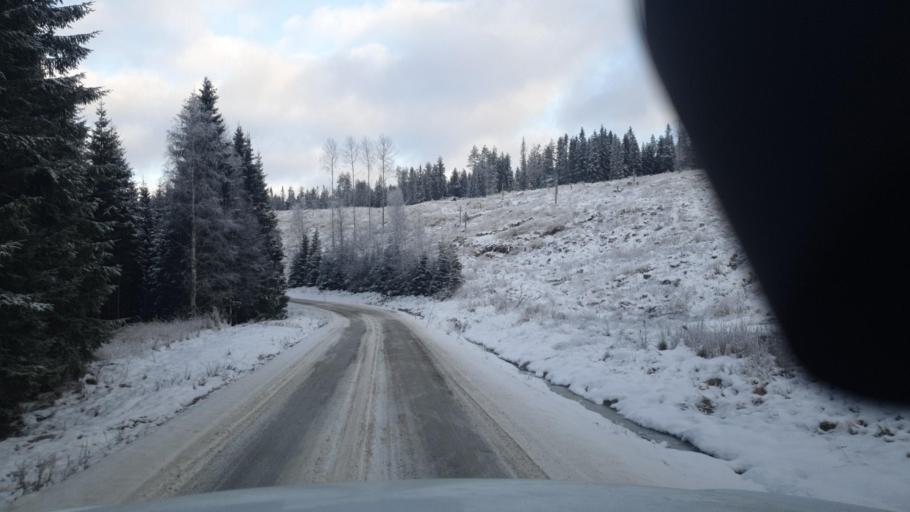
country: SE
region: Vaermland
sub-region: Eda Kommun
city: Charlottenberg
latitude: 60.0398
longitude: 12.6302
